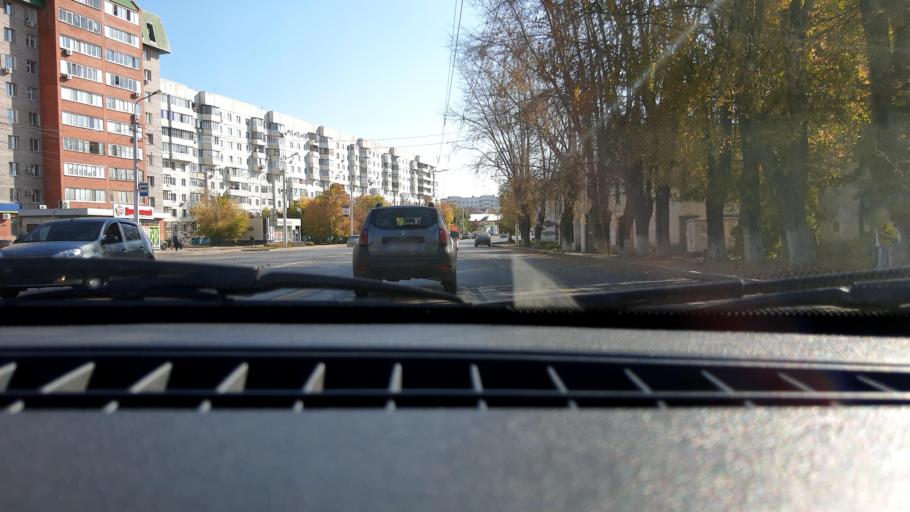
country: RU
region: Bashkortostan
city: Mikhaylovka
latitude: 54.7875
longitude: 55.8832
